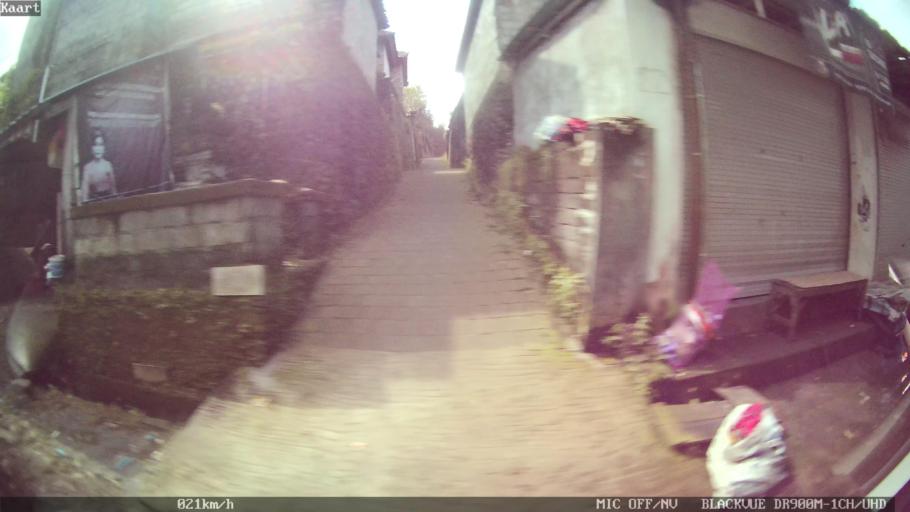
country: ID
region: Bali
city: Banjar Pesalakan
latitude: -8.5064
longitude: 115.3088
